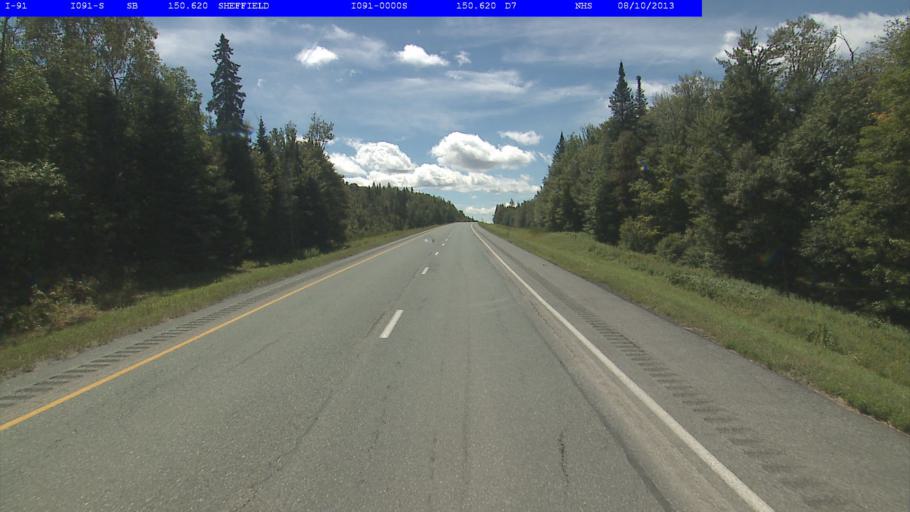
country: US
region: Vermont
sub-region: Caledonia County
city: Lyndonville
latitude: 44.6735
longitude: -72.1329
